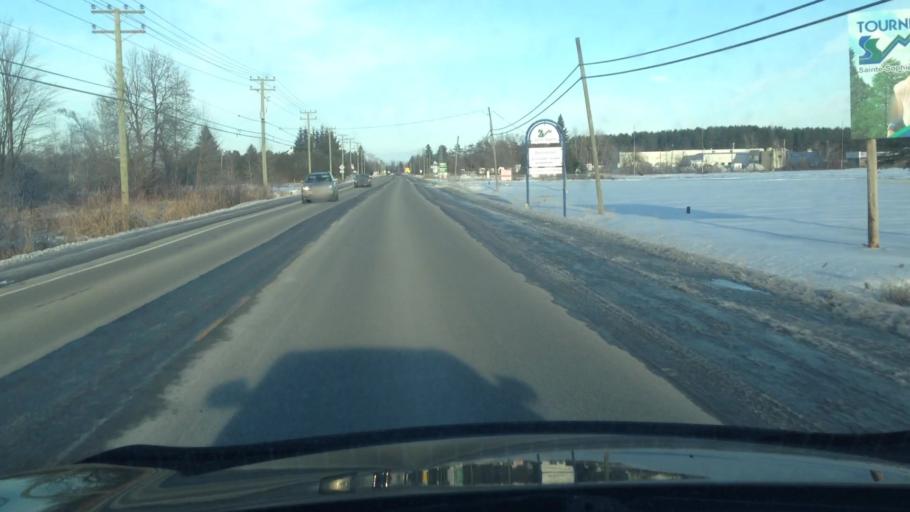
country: CA
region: Quebec
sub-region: Laurentides
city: Sainte-Sophie
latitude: 45.7893
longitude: -73.9477
